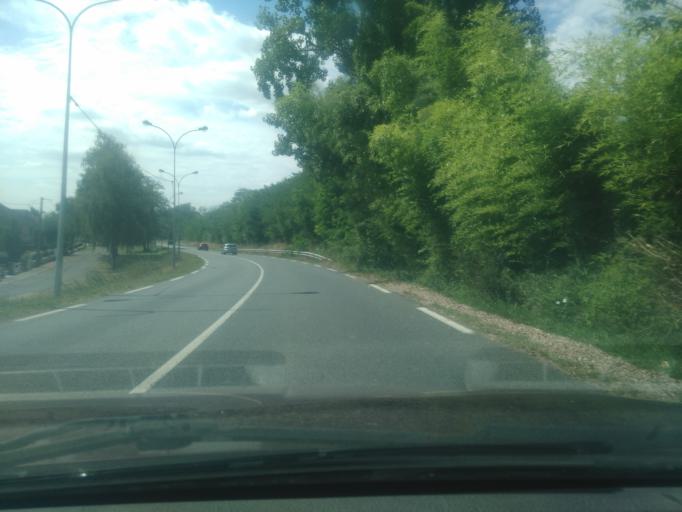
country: FR
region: Bourgogne
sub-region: Departement de la Nievre
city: Saint-Leger-des-Vignes
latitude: 46.8410
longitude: 3.4430
